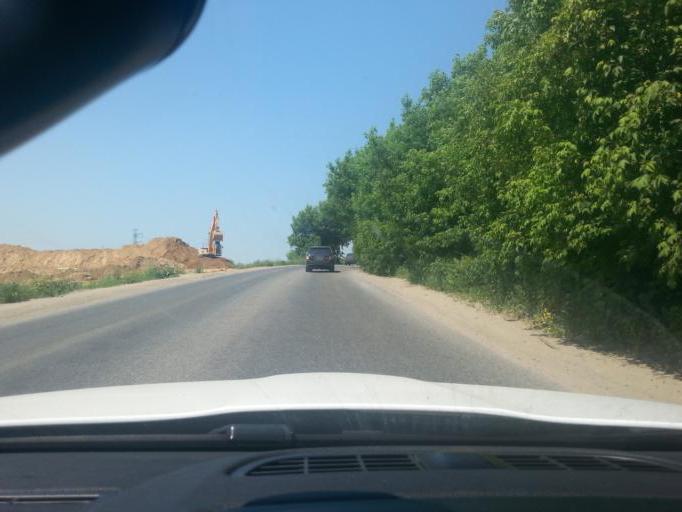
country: RU
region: Moscow
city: Nekrasovka
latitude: 55.7105
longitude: 37.9383
